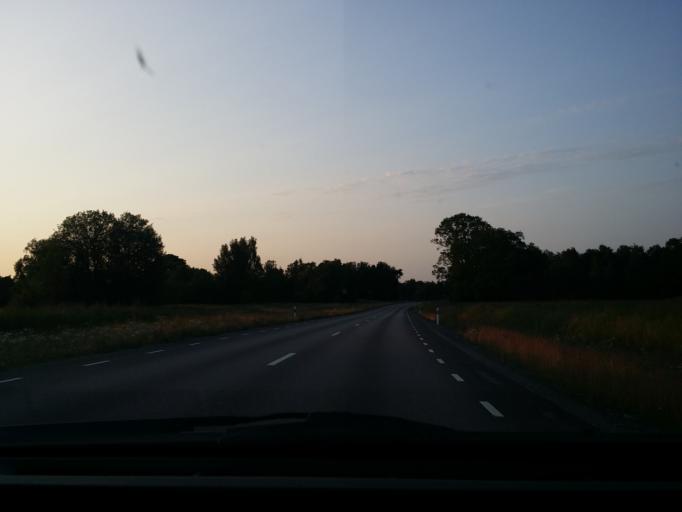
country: SE
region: Vaestmanland
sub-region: Vasteras
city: Tillberga
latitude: 59.5968
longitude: 16.6651
